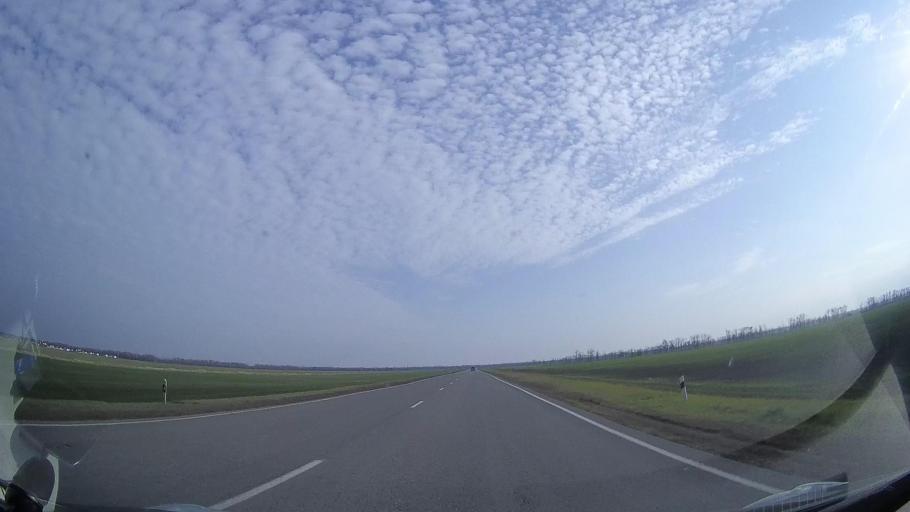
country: RU
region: Rostov
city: Tselina
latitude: 46.5139
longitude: 41.0436
